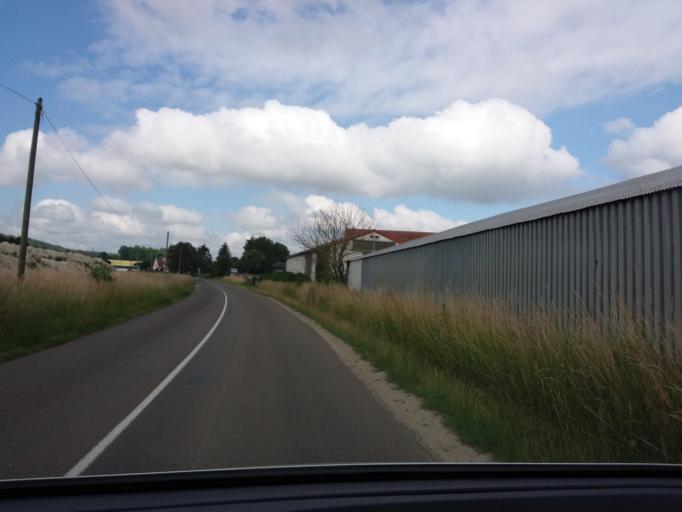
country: FR
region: Champagne-Ardenne
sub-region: Departement de la Marne
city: Fismes
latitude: 49.3782
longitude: 3.6887
